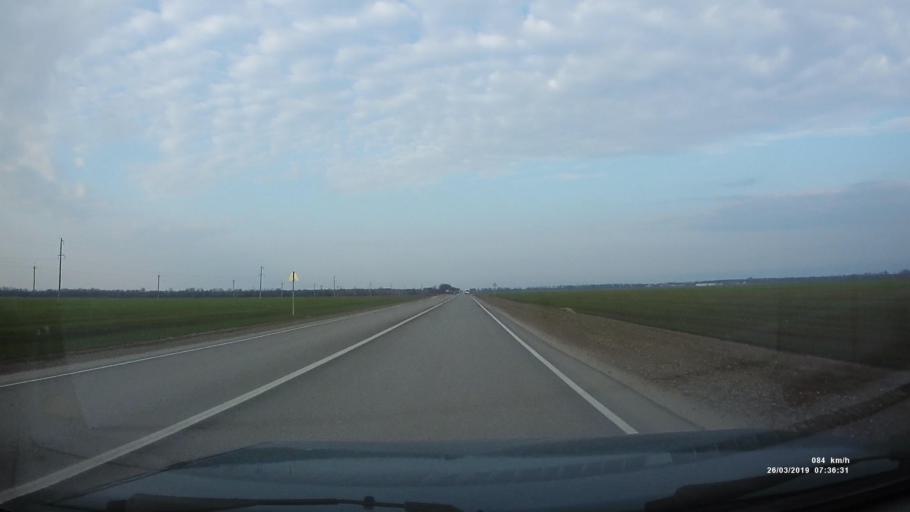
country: RU
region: Rostov
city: Novobessergenovka
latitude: 47.2049
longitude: 38.7186
